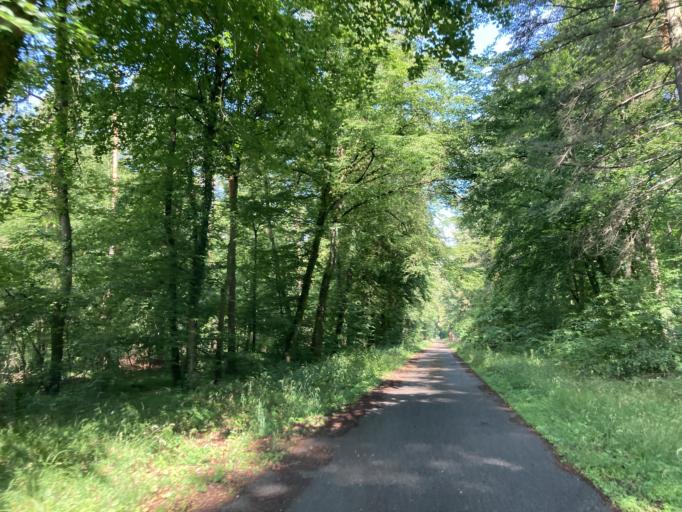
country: DE
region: Baden-Wuerttemberg
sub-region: Karlsruhe Region
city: Graben-Neudorf
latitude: 49.1612
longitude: 8.5129
